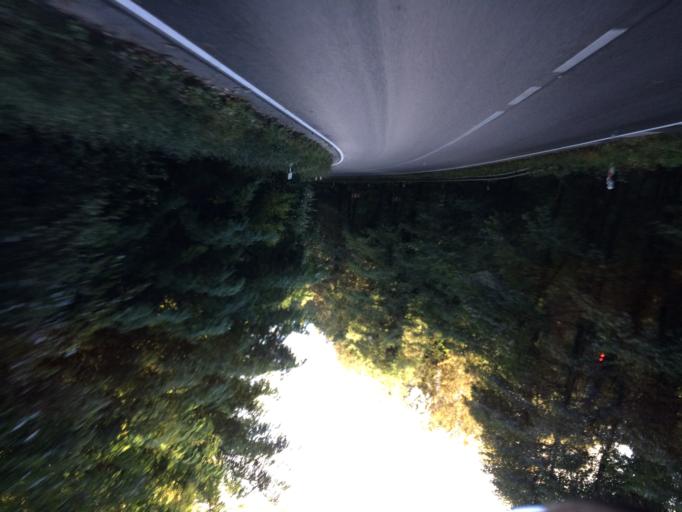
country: DE
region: North Rhine-Westphalia
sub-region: Regierungsbezirk Koln
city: Bad Honnef
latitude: 50.6787
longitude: 7.2267
